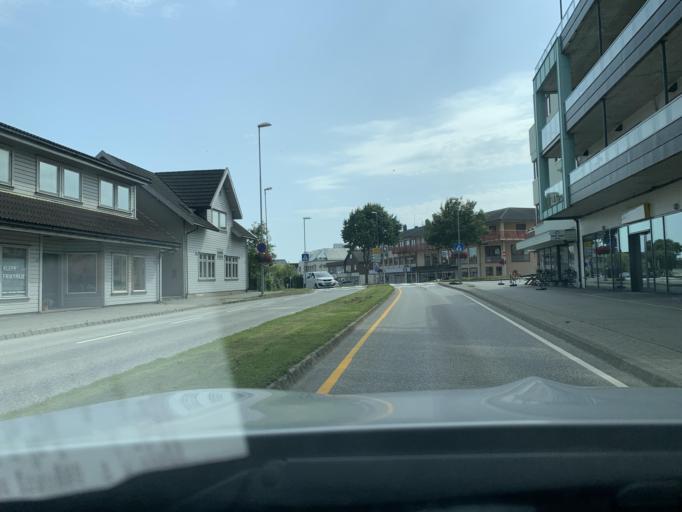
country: NO
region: Rogaland
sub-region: Klepp
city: Kleppe
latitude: 58.7749
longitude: 5.6293
